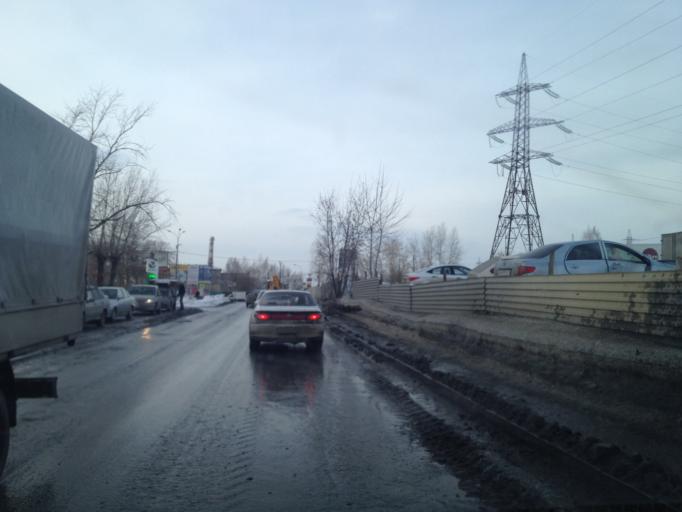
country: RU
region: Sverdlovsk
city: Yekaterinburg
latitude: 56.8748
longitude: 60.5556
